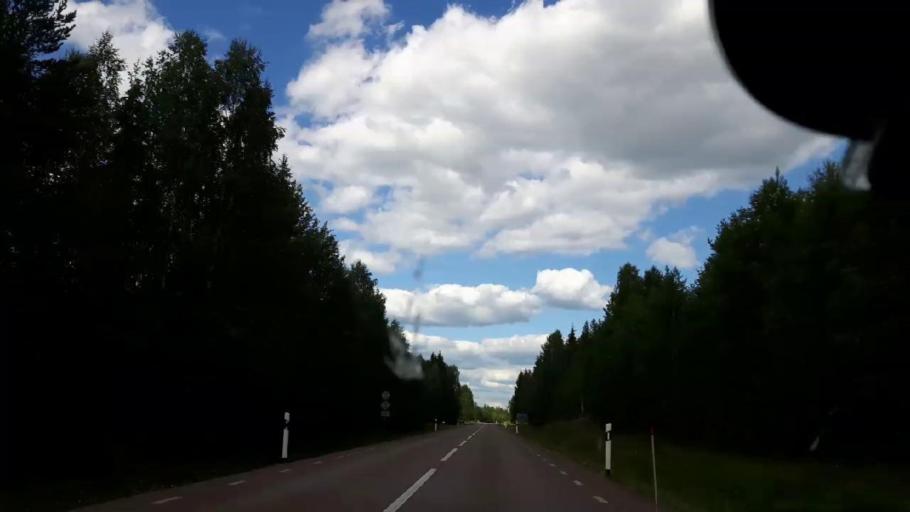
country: SE
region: Jaemtland
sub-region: Ragunda Kommun
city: Hammarstrand
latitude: 62.9270
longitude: 16.6992
